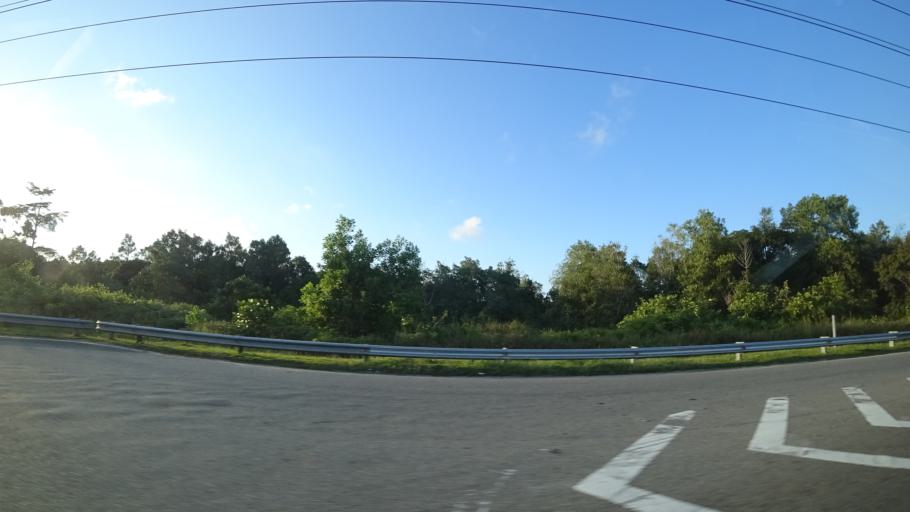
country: BN
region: Tutong
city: Tutong
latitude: 4.7629
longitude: 114.6456
